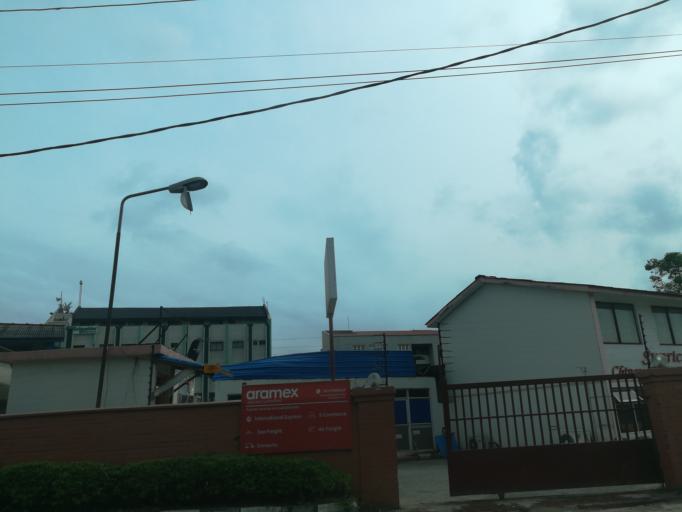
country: NG
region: Lagos
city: Ikeja
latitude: 6.6102
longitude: 3.3455
